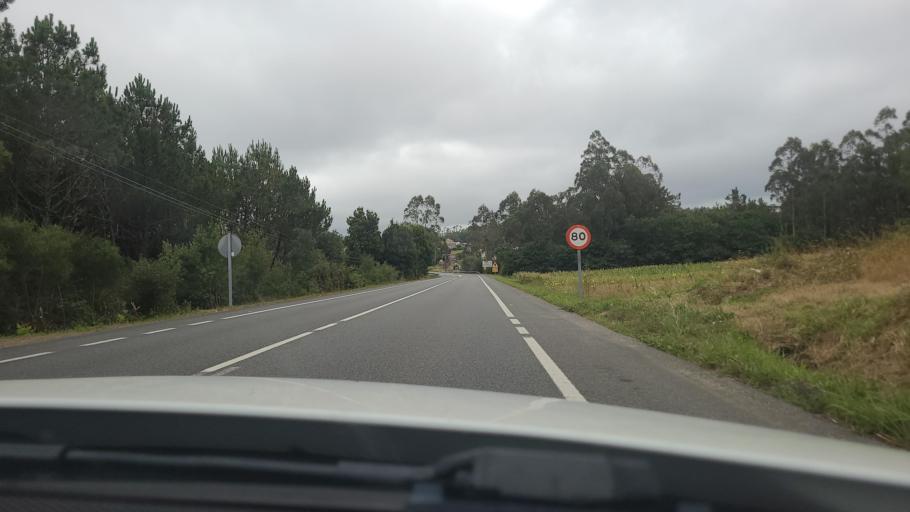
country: ES
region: Galicia
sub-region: Provincia da Coruna
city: Dumbria
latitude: 43.0097
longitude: -9.1648
